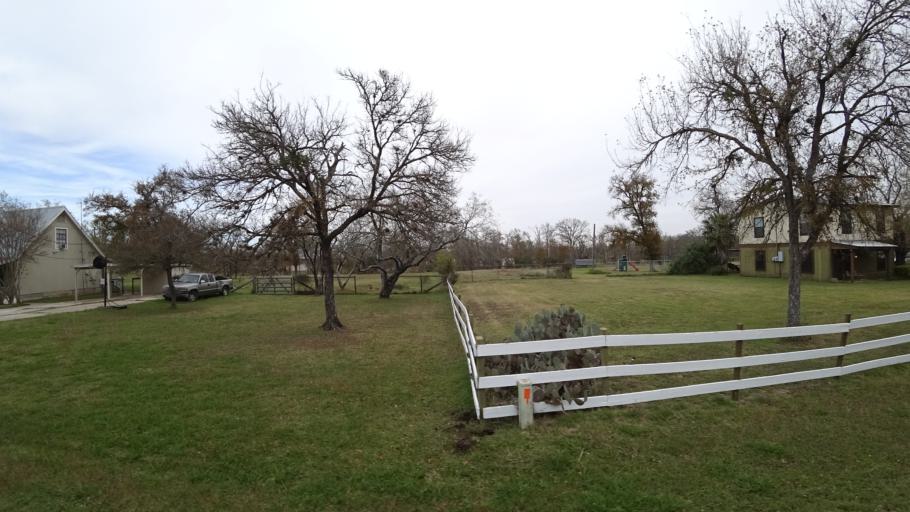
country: US
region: Texas
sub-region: Travis County
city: Garfield
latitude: 30.1072
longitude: -97.5747
